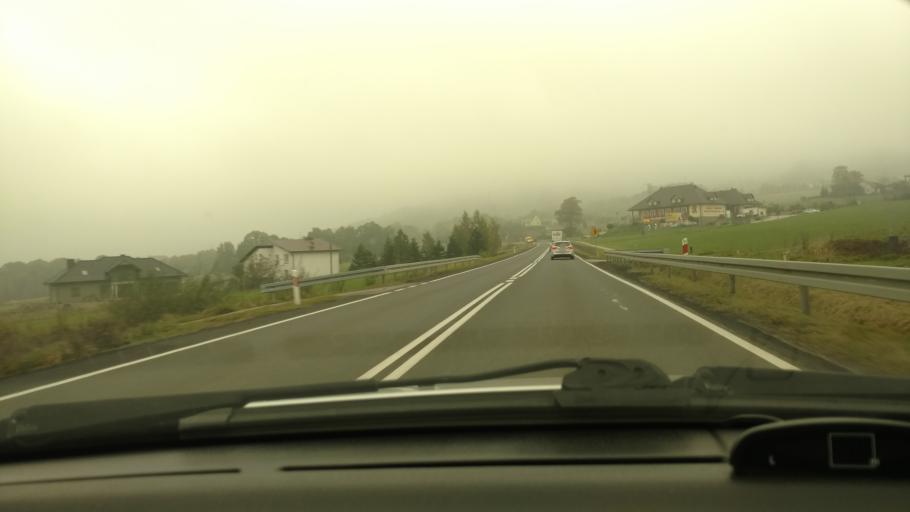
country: PL
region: Lesser Poland Voivodeship
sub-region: Powiat nowosadecki
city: Kamionka Wielka
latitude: 49.6149
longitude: 20.8701
